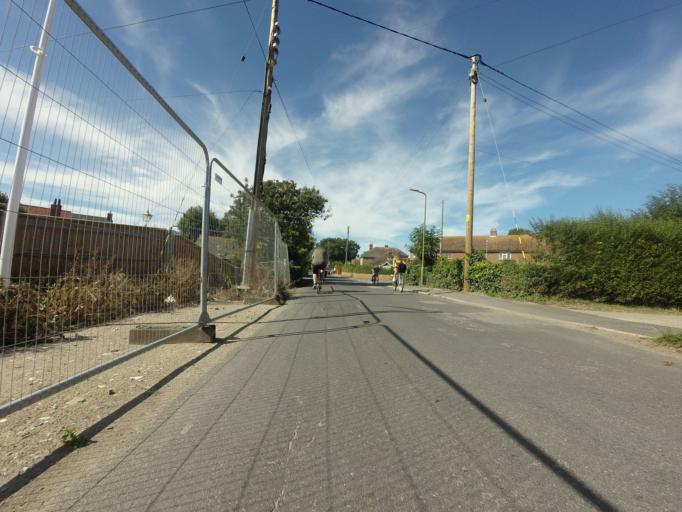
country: GB
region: England
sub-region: Kent
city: Birchington-on-Sea
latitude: 51.3516
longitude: 1.2544
